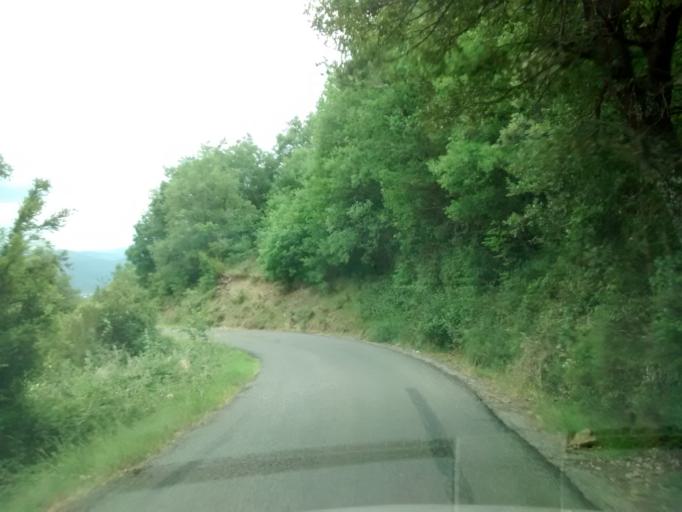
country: ES
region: Aragon
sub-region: Provincia de Huesca
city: Puertolas
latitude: 42.5406
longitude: 0.1333
